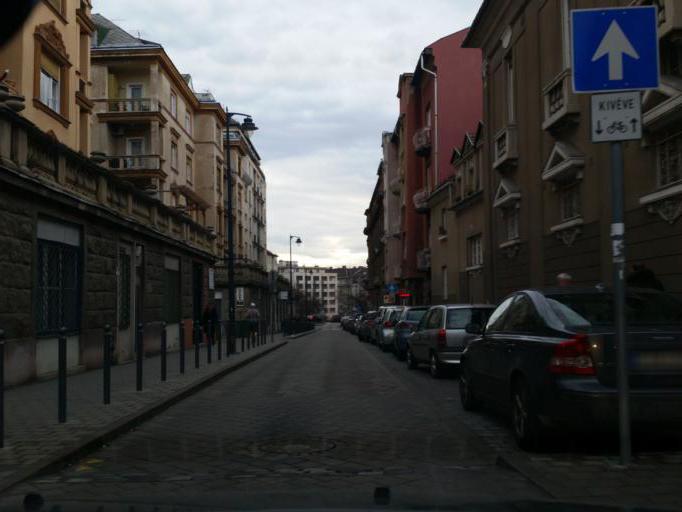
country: HU
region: Budapest
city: Budapest II. keruelet
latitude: 47.5121
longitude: 19.0284
